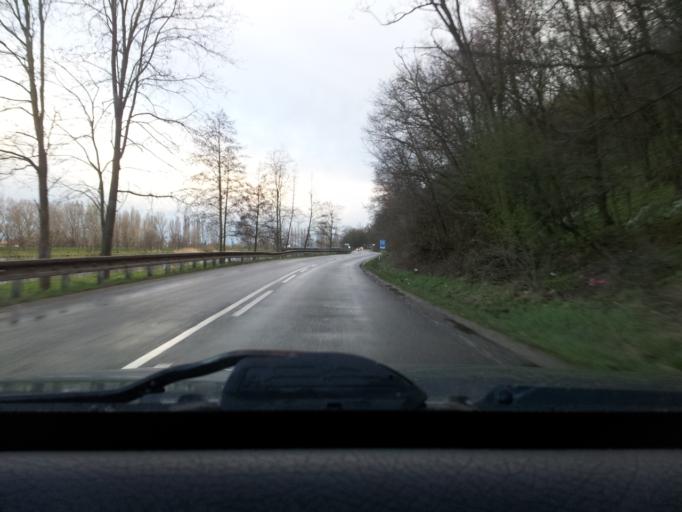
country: SK
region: Nitriansky
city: Tlmace
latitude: 48.2953
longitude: 18.5286
